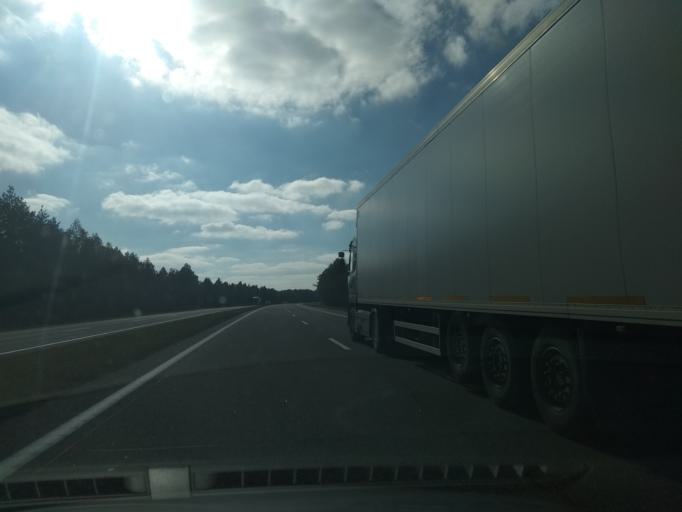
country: BY
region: Brest
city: Baranovichi
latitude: 53.0737
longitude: 25.8825
